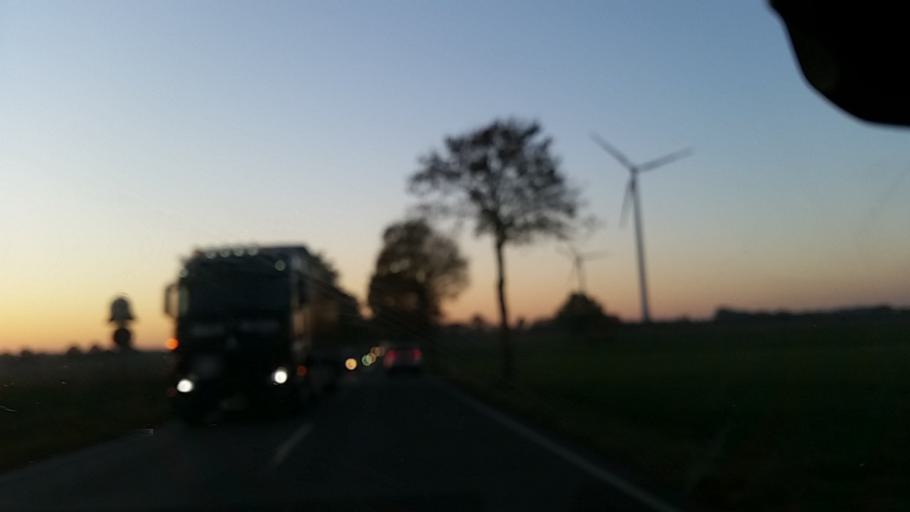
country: DE
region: Lower Saxony
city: Uelzen
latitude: 52.9443
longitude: 10.5893
